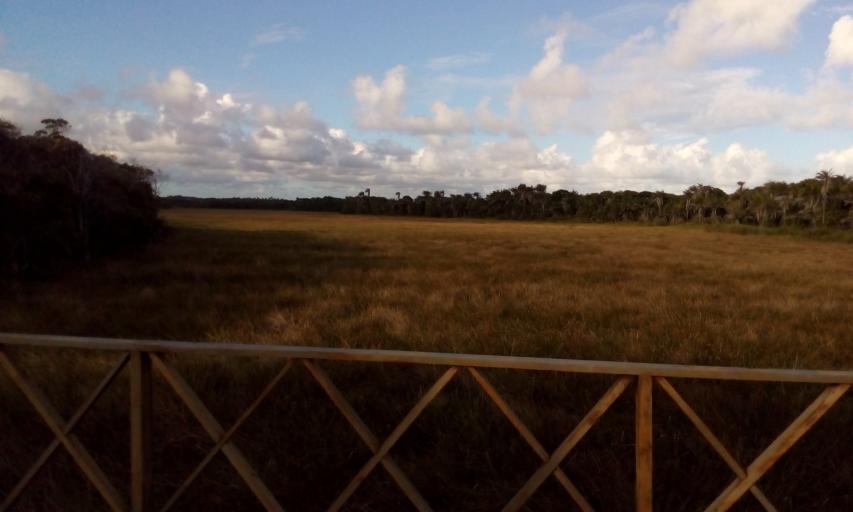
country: BR
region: Bahia
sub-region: Mata De Sao Joao
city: Mata de Sao Joao
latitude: -12.5618
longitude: -37.9994
